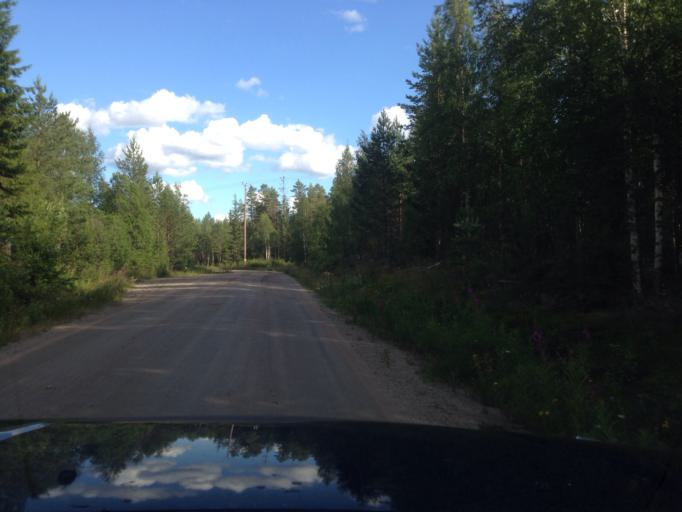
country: SE
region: Dalarna
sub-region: Ludvika Kommun
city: Abborrberget
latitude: 60.3105
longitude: 14.6698
